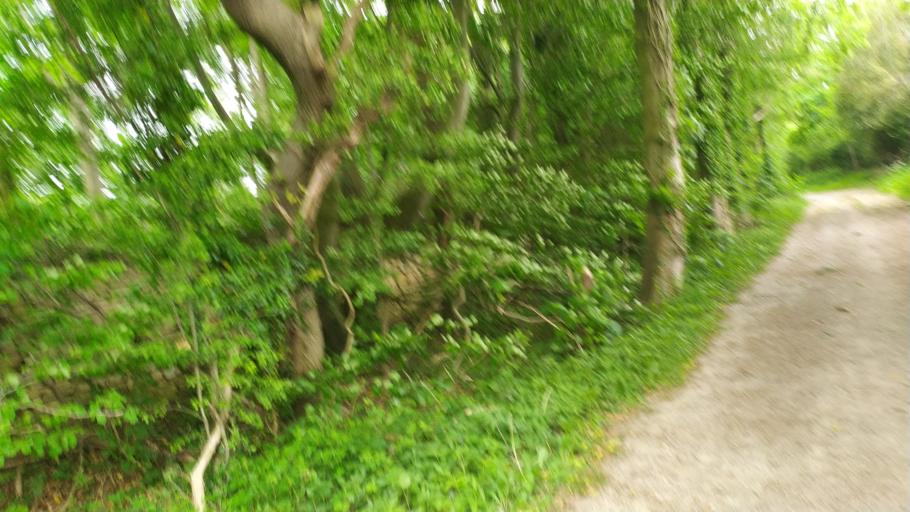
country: GB
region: England
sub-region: City and Borough of Leeds
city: Thorner
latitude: 53.8625
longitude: -1.3963
